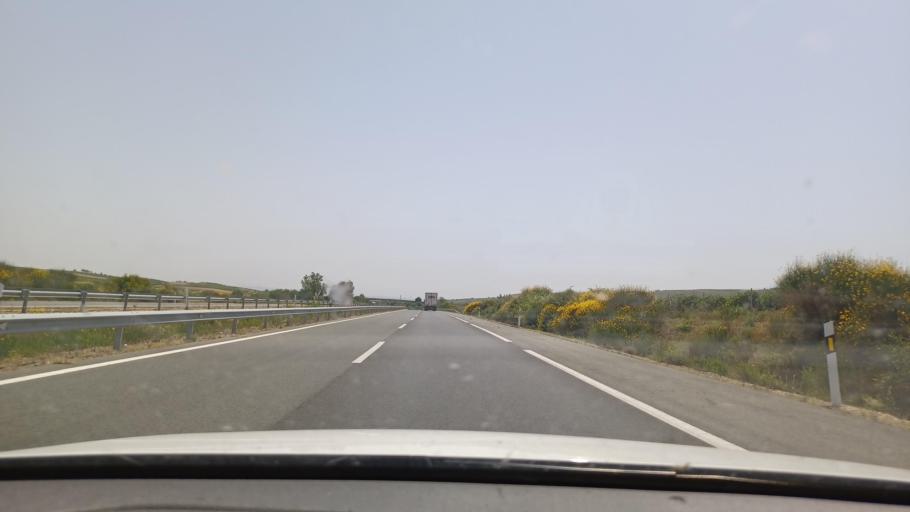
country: ES
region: La Rioja
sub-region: Provincia de La Rioja
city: Alcanadre
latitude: 42.3852
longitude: -2.1185
